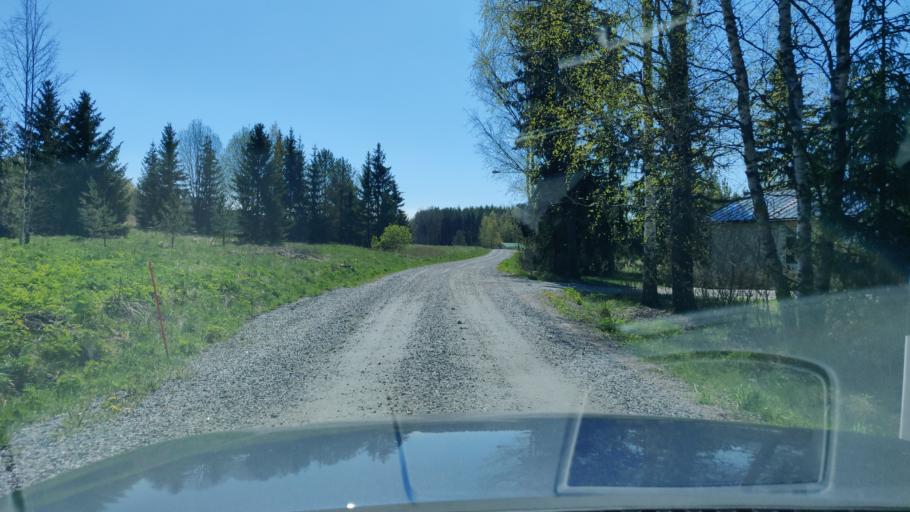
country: FI
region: Uusimaa
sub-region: Helsinki
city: Nurmijaervi
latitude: 60.3594
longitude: 24.7564
